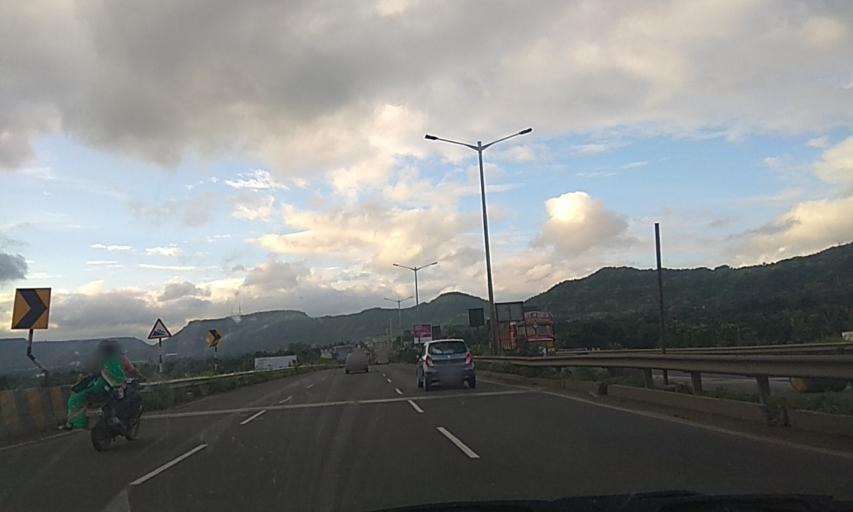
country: IN
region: Maharashtra
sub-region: Satara Division
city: Satara
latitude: 17.6287
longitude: 74.0155
